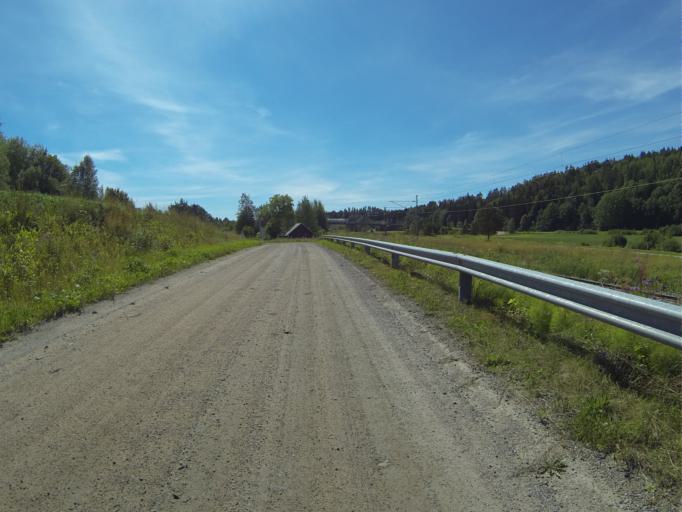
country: FI
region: Varsinais-Suomi
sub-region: Salo
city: Salo
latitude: 60.3078
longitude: 23.1074
